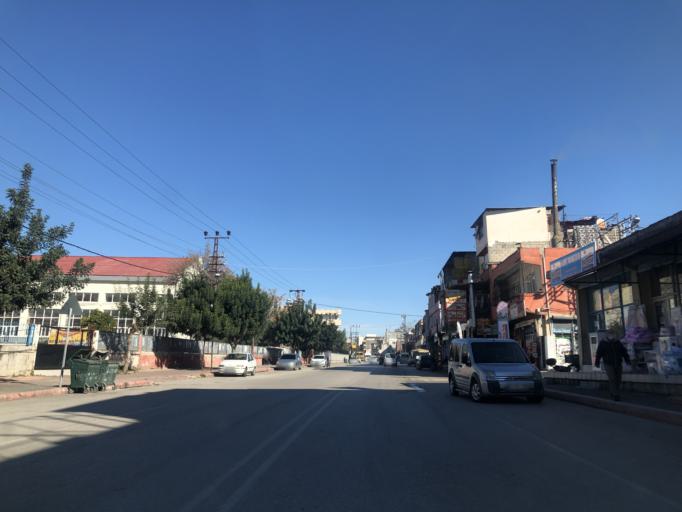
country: TR
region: Adana
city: Yuregir
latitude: 37.0098
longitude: 35.3663
